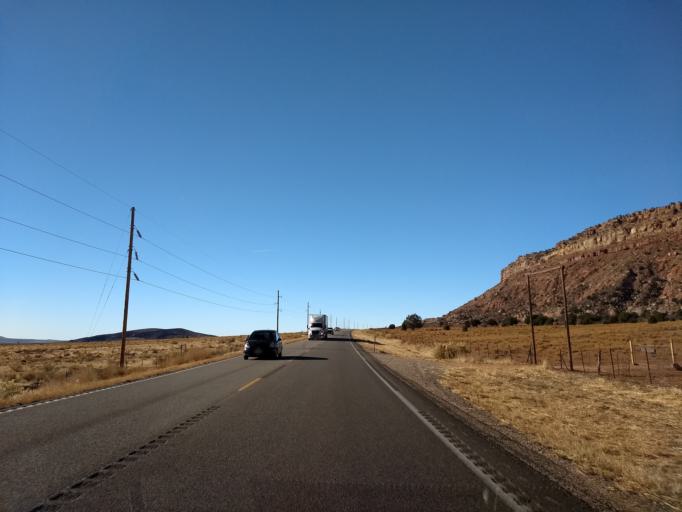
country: US
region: Utah
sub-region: Washington County
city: LaVerkin
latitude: 37.1187
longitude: -113.1725
